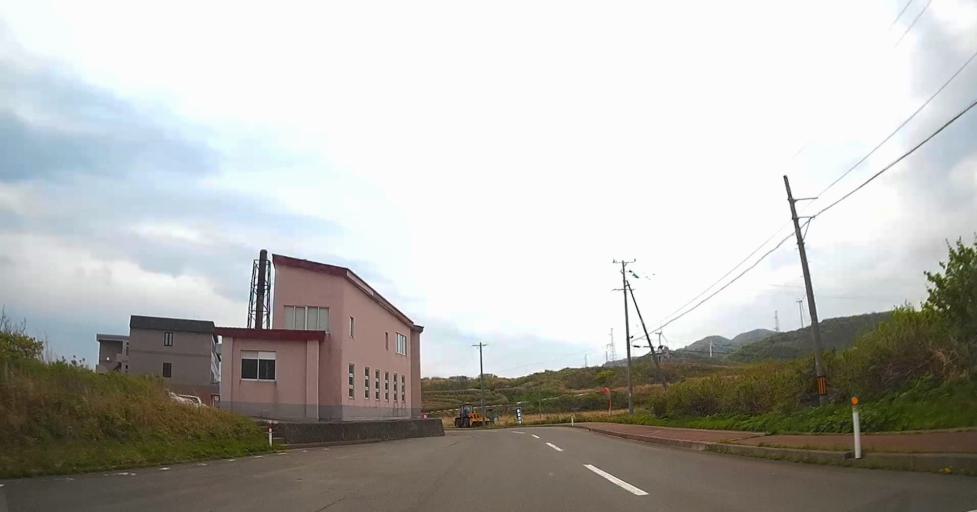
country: JP
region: Aomori
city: Shimokizukuri
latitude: 41.2572
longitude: 140.3464
